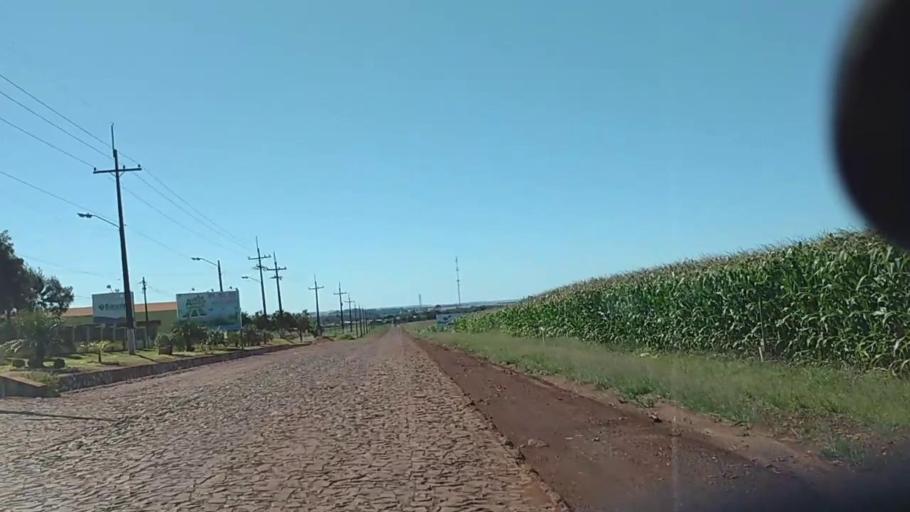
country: PY
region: Alto Parana
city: Naranjal
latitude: -25.9742
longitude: -55.2116
